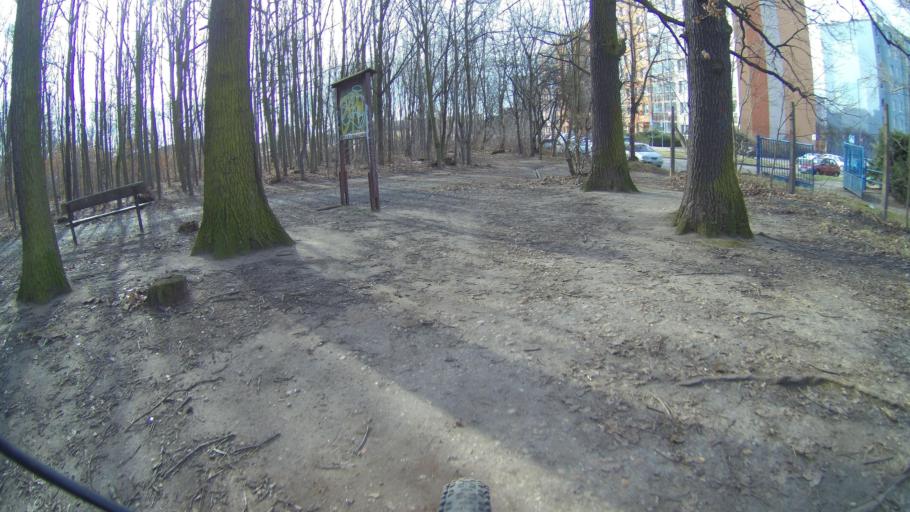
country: CZ
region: Praha
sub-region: Praha 8
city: Karlin
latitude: 50.1293
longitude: 14.4344
